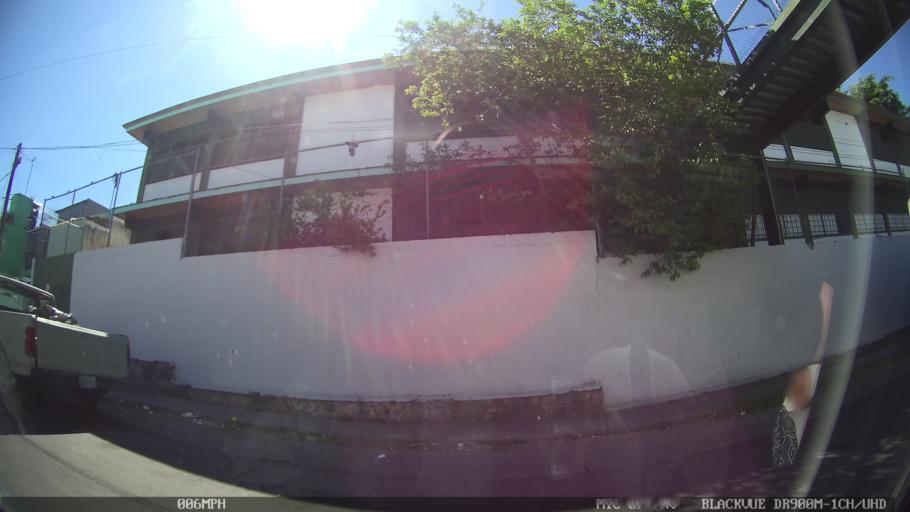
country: MX
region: Jalisco
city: Tlaquepaque
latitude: 20.6967
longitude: -103.2868
